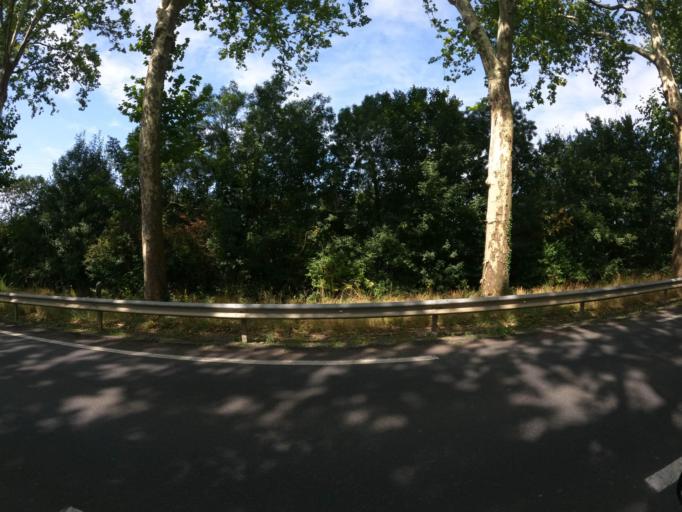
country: FR
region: Poitou-Charentes
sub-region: Departement des Deux-Sevres
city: Frontenay-Rohan-Rohan
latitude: 46.2672
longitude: -0.5294
